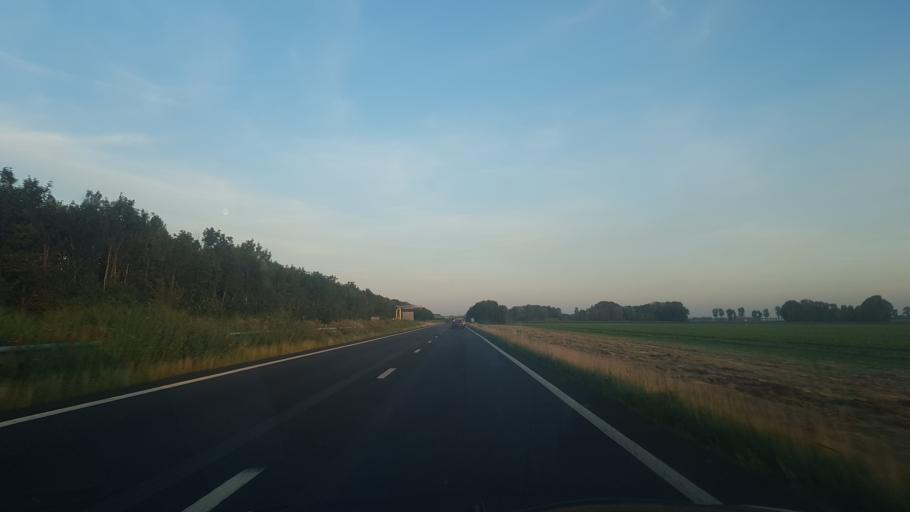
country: NL
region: Flevoland
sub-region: Gemeente Noordoostpolder
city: Emmeloord
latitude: 52.6759
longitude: 5.7859
